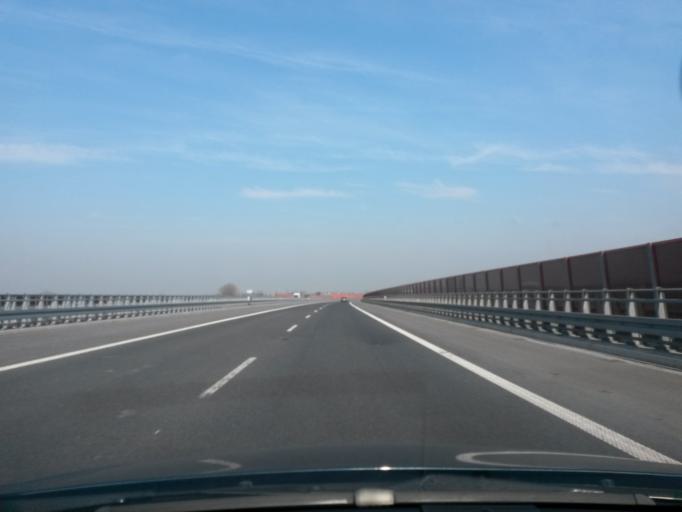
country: PL
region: Lodz Voivodeship
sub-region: Powiat kutnowski
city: Krzyzanow
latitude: 52.1352
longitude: 19.4865
